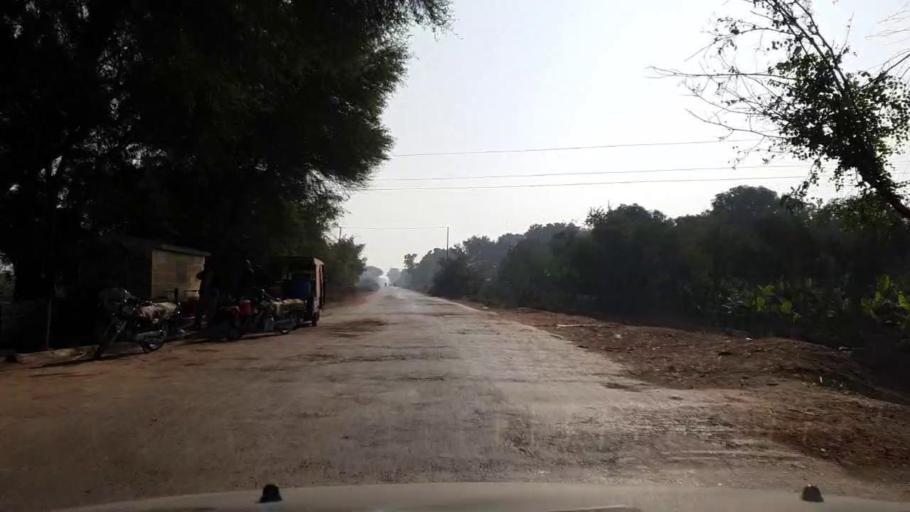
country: PK
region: Sindh
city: Matiari
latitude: 25.5975
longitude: 68.4604
